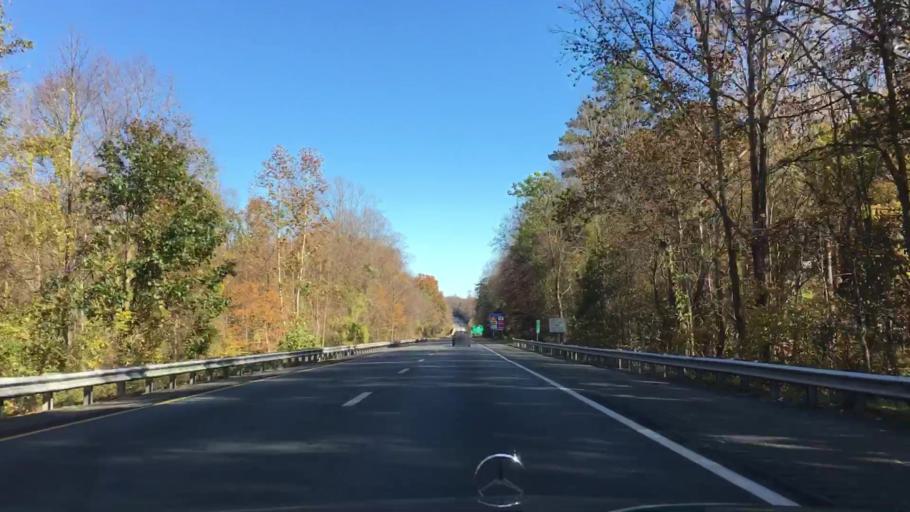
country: US
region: Virginia
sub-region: City of Charlottesville
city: Charlottesville
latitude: 38.0157
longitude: -78.4577
